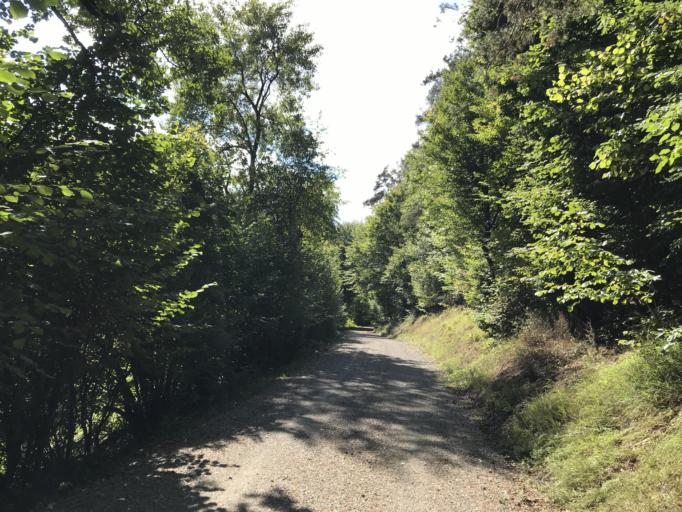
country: DE
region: Hesse
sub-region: Regierungsbezirk Kassel
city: Sachsenhausen
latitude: 51.2232
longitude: 9.0297
